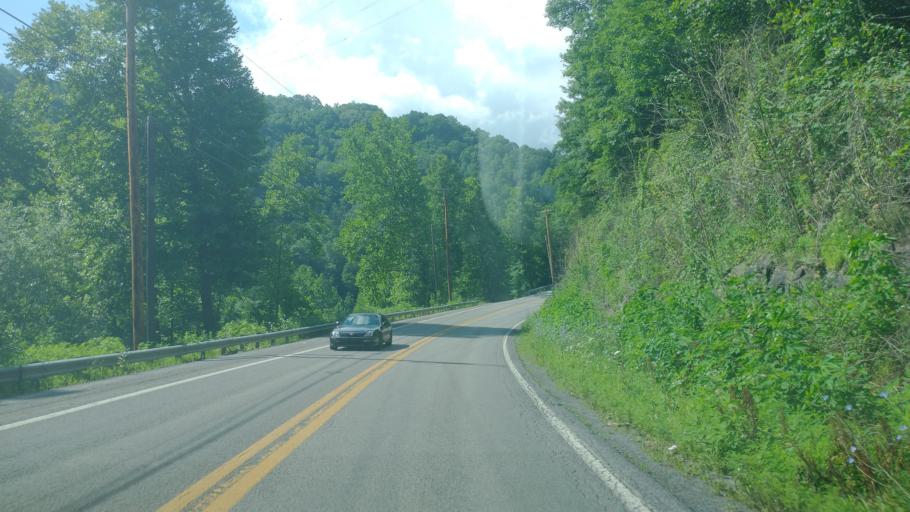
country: US
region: West Virginia
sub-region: McDowell County
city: Welch
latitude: 37.4232
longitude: -81.5113
